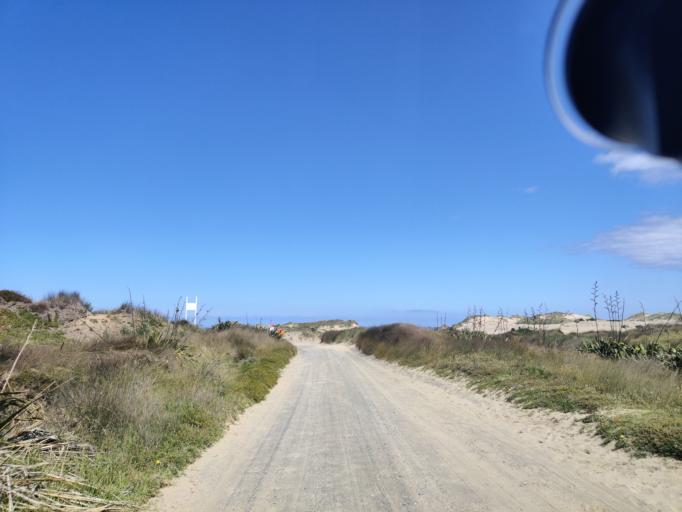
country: NZ
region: Northland
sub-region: Far North District
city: Kaitaia
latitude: -34.8981
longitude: 173.0864
